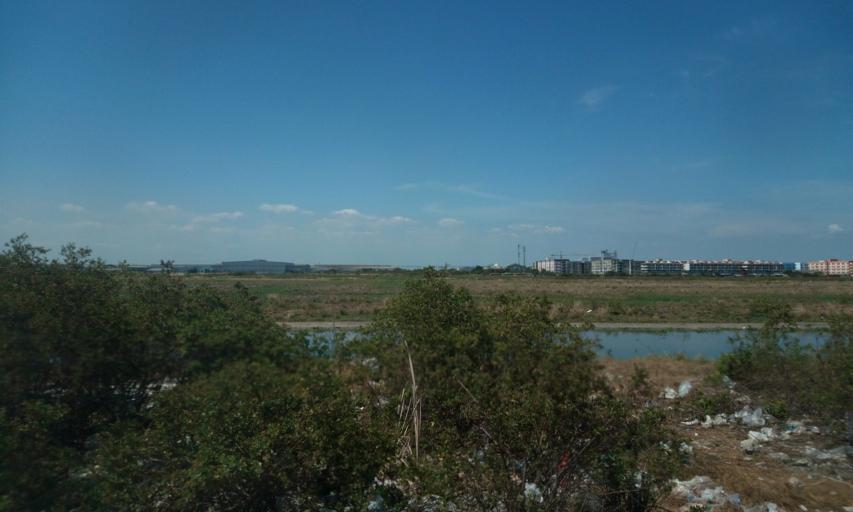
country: TH
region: Samut Prakan
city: Bang Bo District
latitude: 13.5548
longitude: 100.7755
